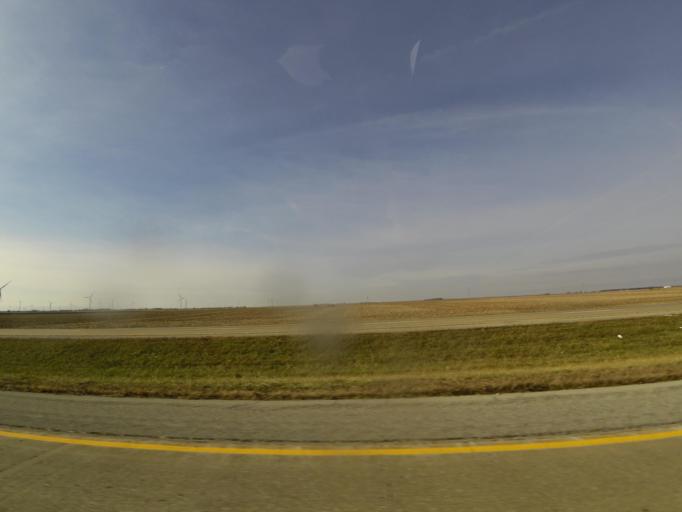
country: US
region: Illinois
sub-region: Macon County
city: Maroa
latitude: 40.0633
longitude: -88.9656
